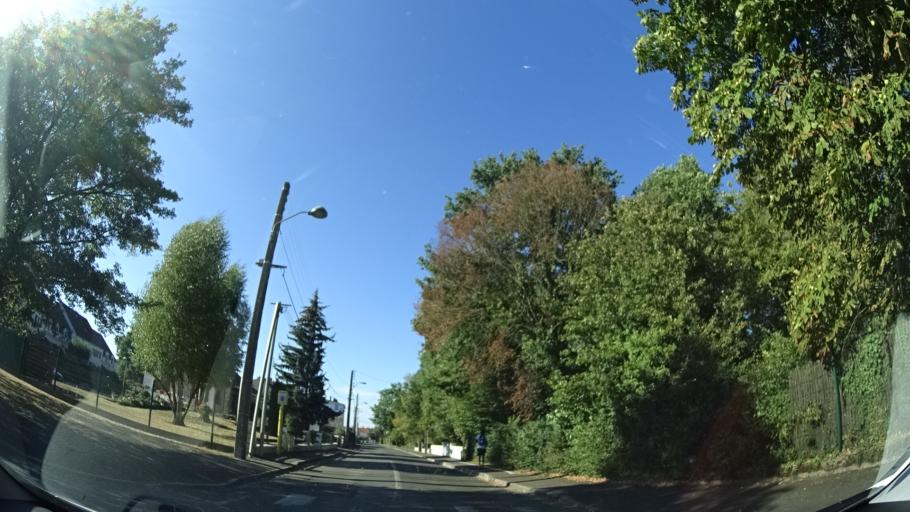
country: FR
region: Centre
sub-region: Departement du Loiret
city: Saint-Jean-de-Braye
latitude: 47.9148
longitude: 1.9641
